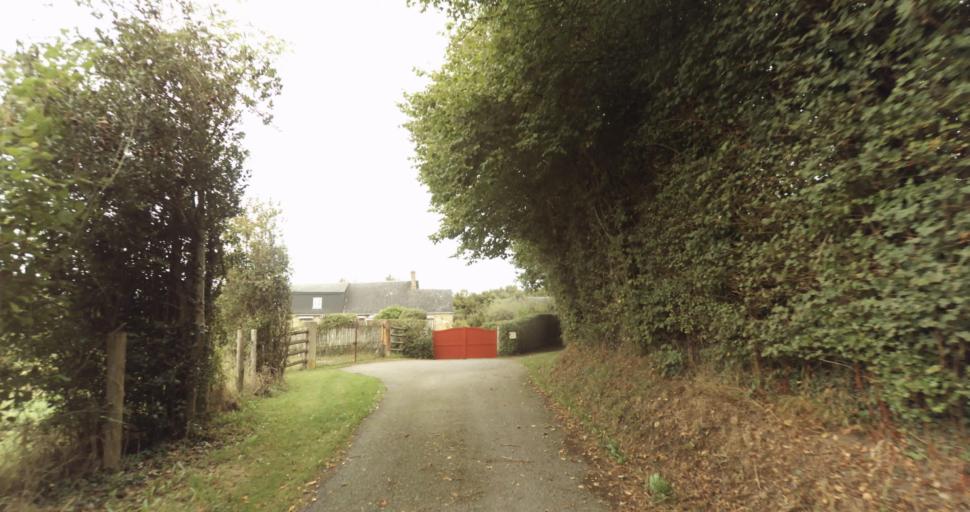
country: FR
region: Lower Normandy
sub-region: Departement de l'Orne
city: Gace
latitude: 48.6753
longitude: 0.3166
